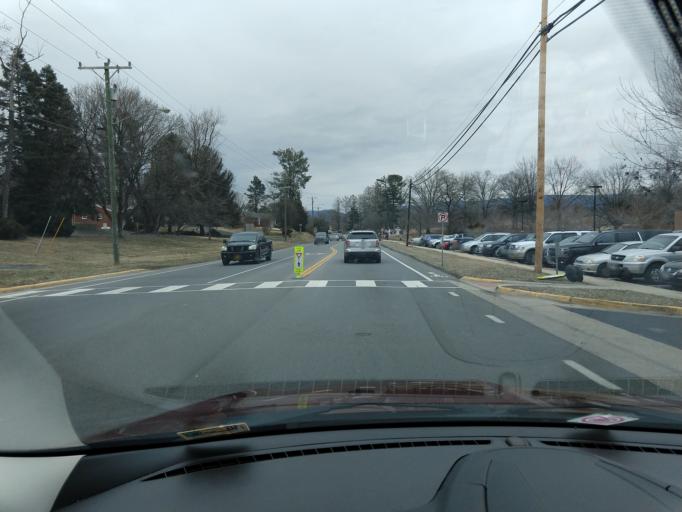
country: US
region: Virginia
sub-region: City of Waynesboro
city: Waynesboro
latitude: 38.0702
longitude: -78.9112
